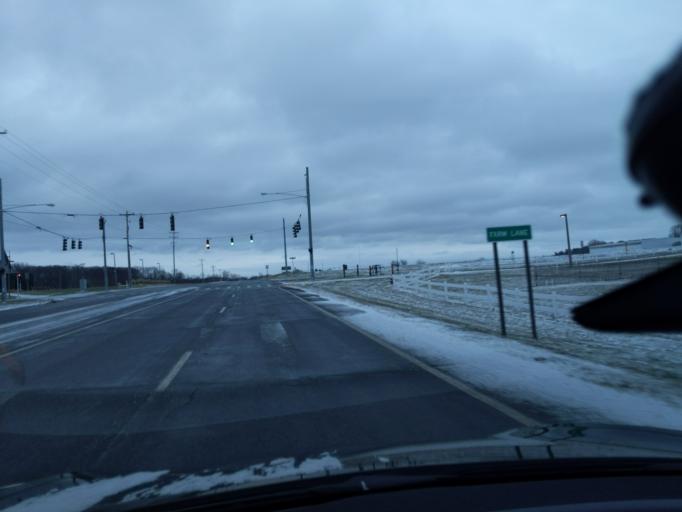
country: US
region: Michigan
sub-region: Ingham County
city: East Lansing
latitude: 42.7118
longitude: -84.4791
